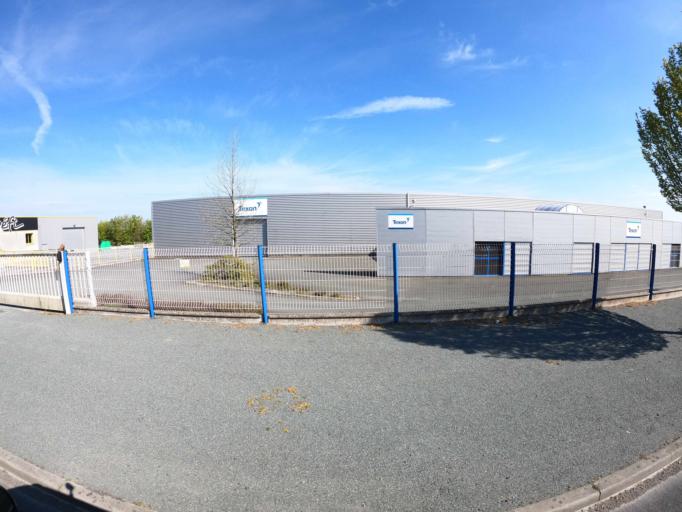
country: FR
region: Pays de la Loire
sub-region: Departement de Maine-et-Loire
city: La Seguiniere
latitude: 47.0728
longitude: -0.9353
